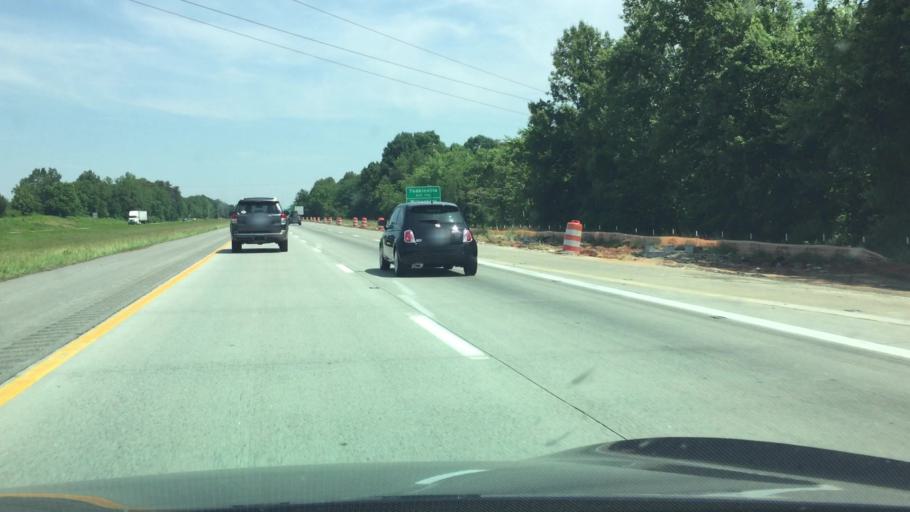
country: US
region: North Carolina
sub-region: Yadkin County
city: Jonesville
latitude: 36.1091
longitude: -80.8134
